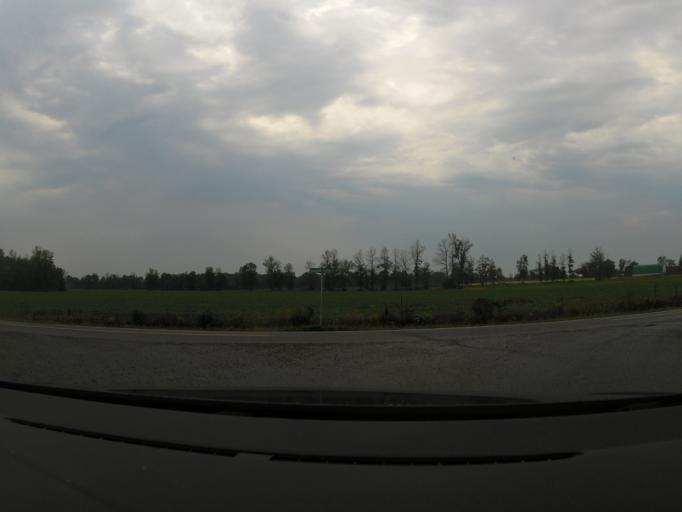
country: CA
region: Ontario
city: Carleton Place
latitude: 45.1753
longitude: -76.1038
